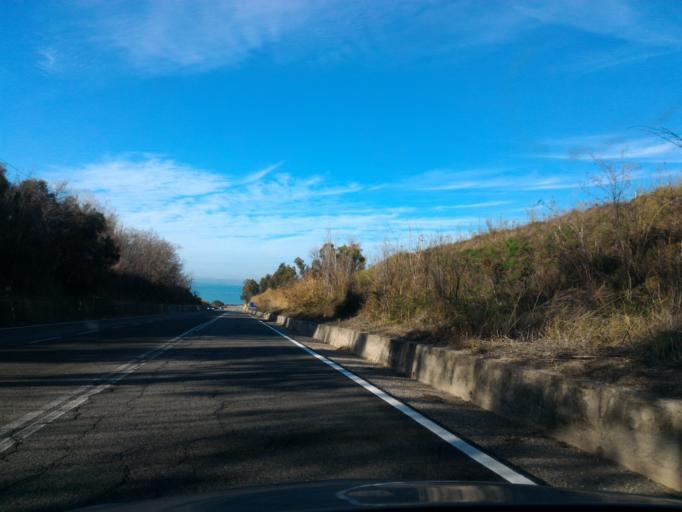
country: IT
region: Calabria
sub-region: Provincia di Crotone
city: Le Castella
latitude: 38.9380
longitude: 16.9987
